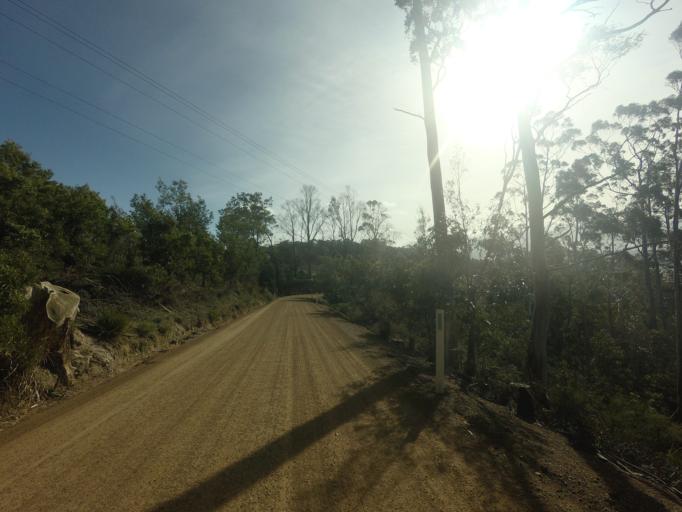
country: AU
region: Tasmania
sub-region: Kingborough
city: Kettering
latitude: -43.0891
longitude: 147.2649
